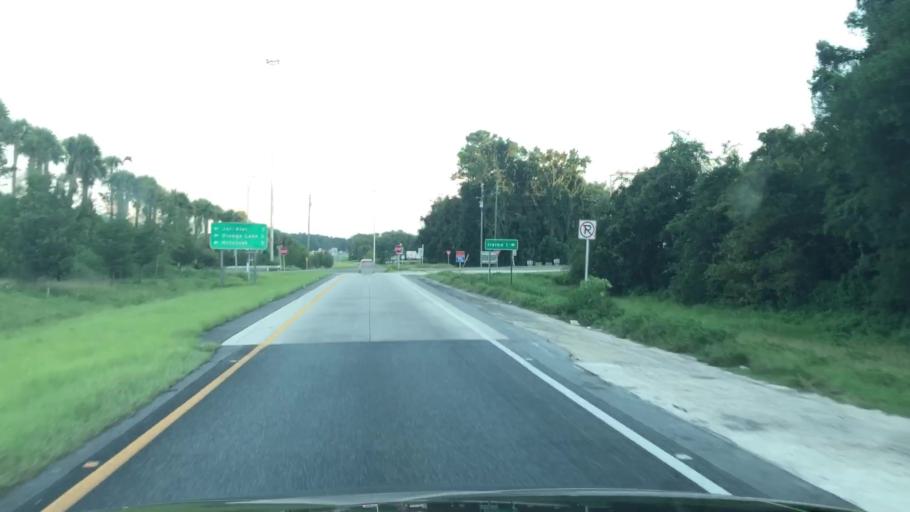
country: US
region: Florida
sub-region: Marion County
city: Citra
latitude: 29.4075
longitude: -82.2487
